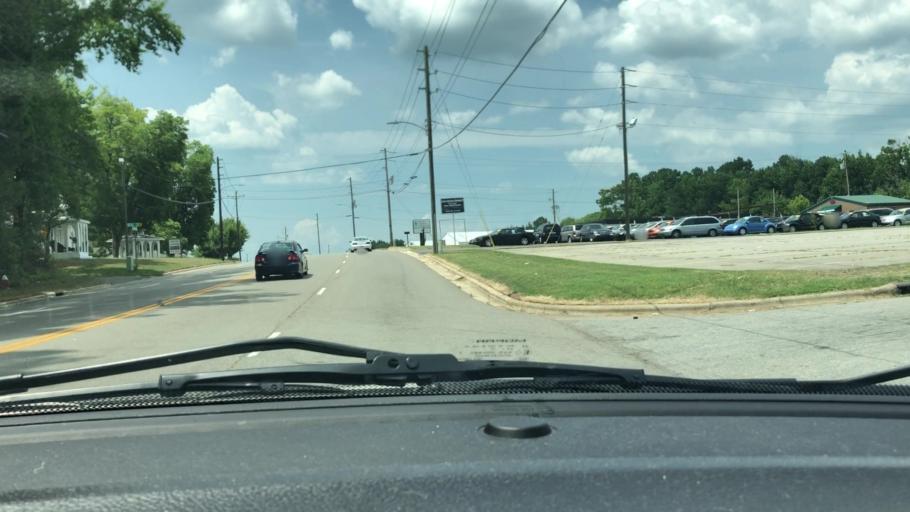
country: US
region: North Carolina
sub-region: Lee County
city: Sanford
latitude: 35.4911
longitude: -79.1899
